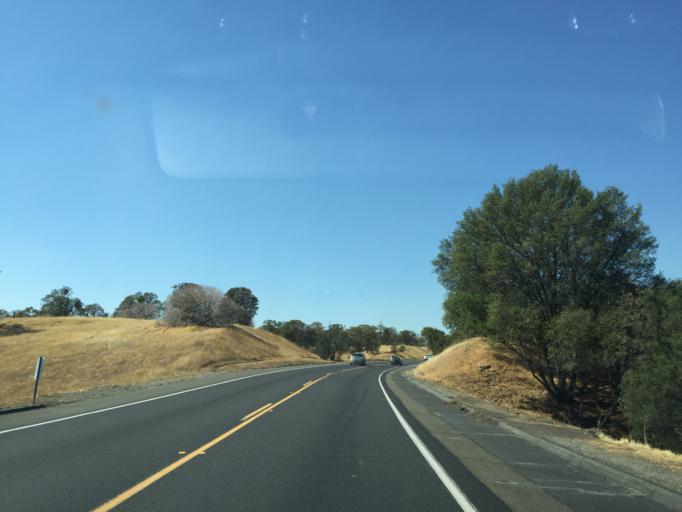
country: US
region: California
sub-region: Tuolumne County
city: Jamestown
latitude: 37.8413
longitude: -120.5143
